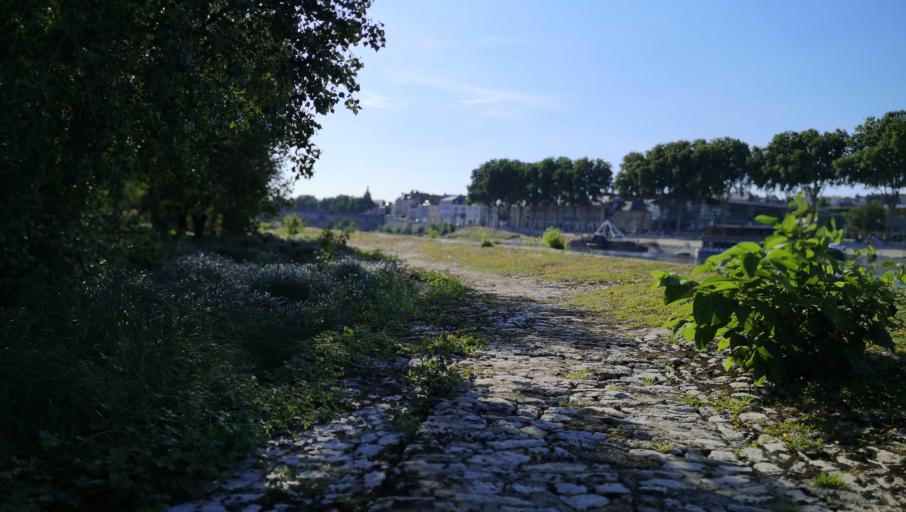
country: FR
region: Centre
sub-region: Departement du Loiret
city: Saint-Jean-le-Blanc
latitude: 47.8964
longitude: 1.9110
